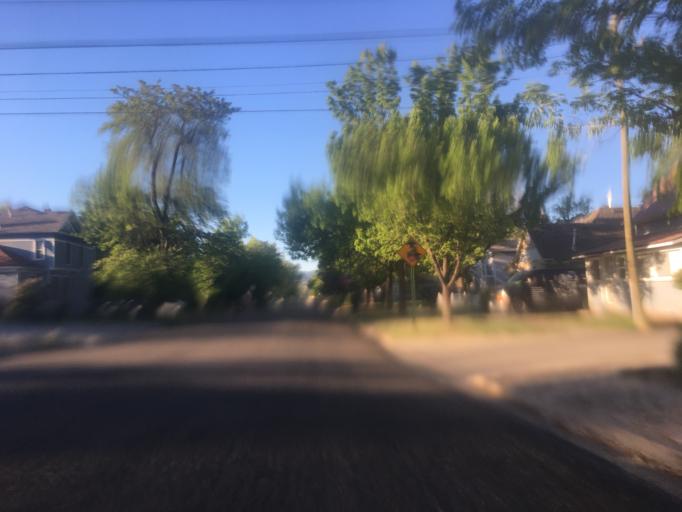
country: US
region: Colorado
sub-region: Mesa County
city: Grand Junction
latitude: 39.0741
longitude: -108.5627
